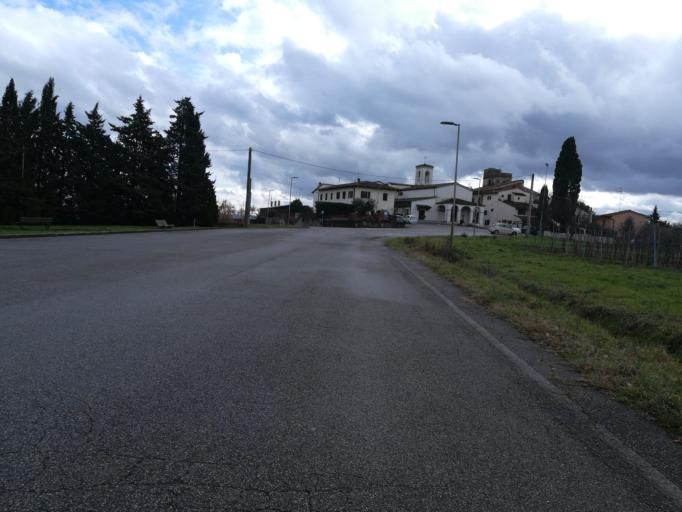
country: IT
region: Tuscany
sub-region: Provincia di Prato
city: Poggio A Caiano
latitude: 43.8072
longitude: 11.0485
